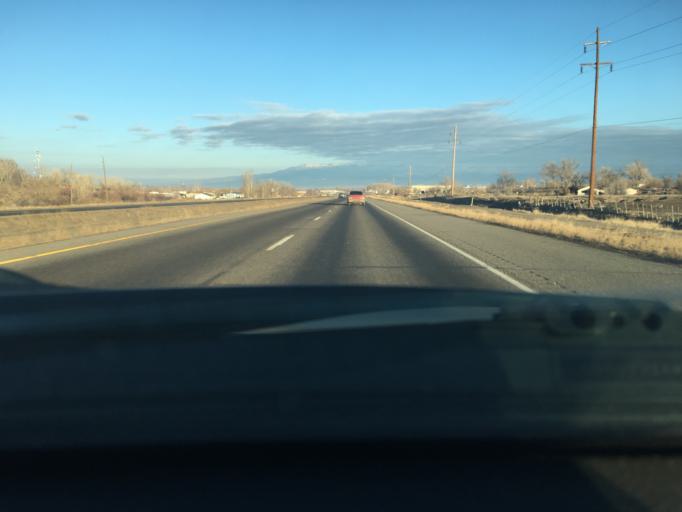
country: US
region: Colorado
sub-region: Montrose County
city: Olathe
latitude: 38.5864
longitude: -107.9677
